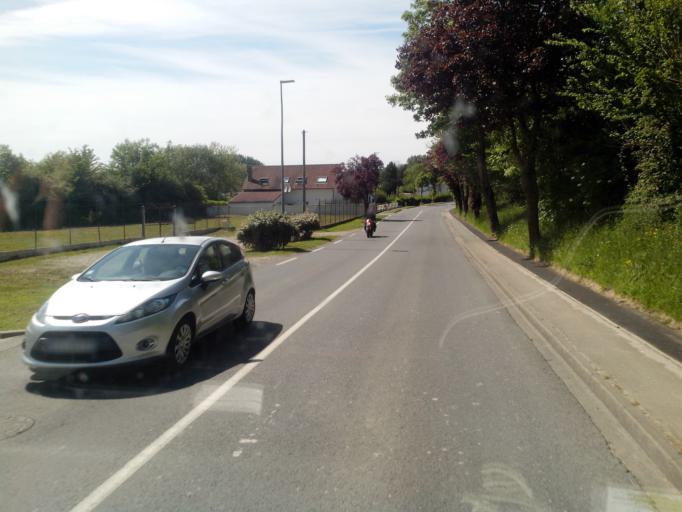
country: FR
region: Nord-Pas-de-Calais
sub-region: Departement du Pas-de-Calais
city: Montreuil
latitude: 50.4837
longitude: 1.7535
